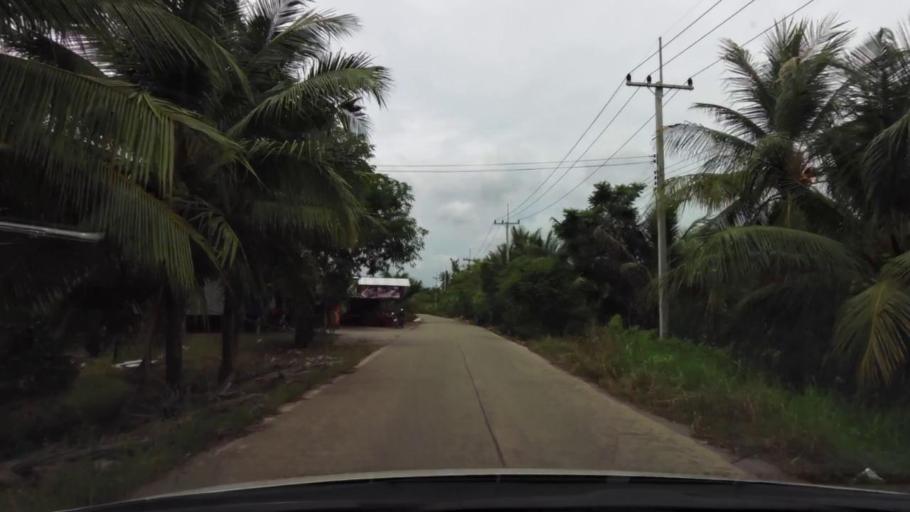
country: TH
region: Ratchaburi
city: Damnoen Saduak
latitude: 13.5690
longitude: 100.0168
